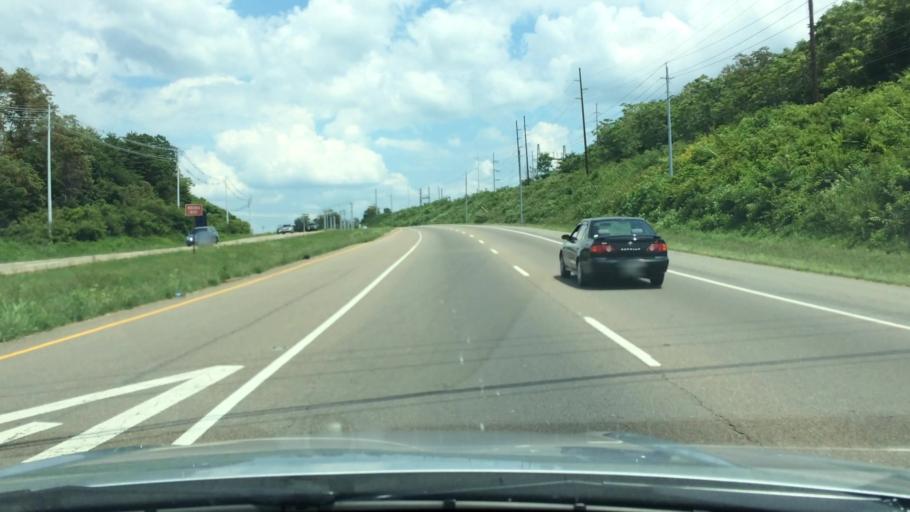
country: US
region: Tennessee
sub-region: Hamblen County
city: Morristown
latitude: 36.1874
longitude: -83.2954
